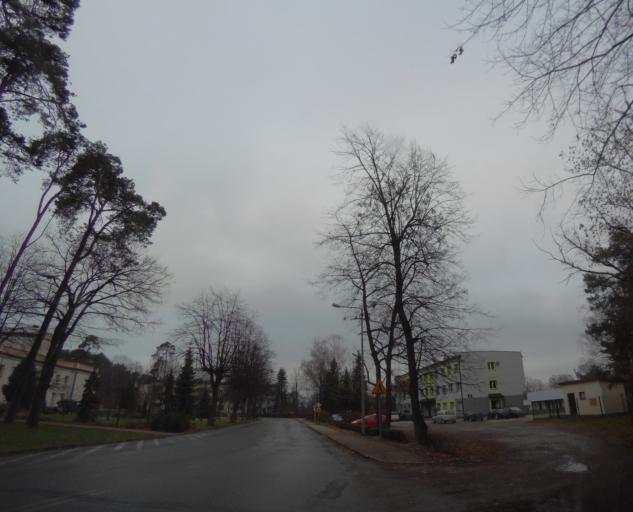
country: PL
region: Subcarpathian Voivodeship
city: Nowa Sarzyna
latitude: 50.3280
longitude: 22.3370
